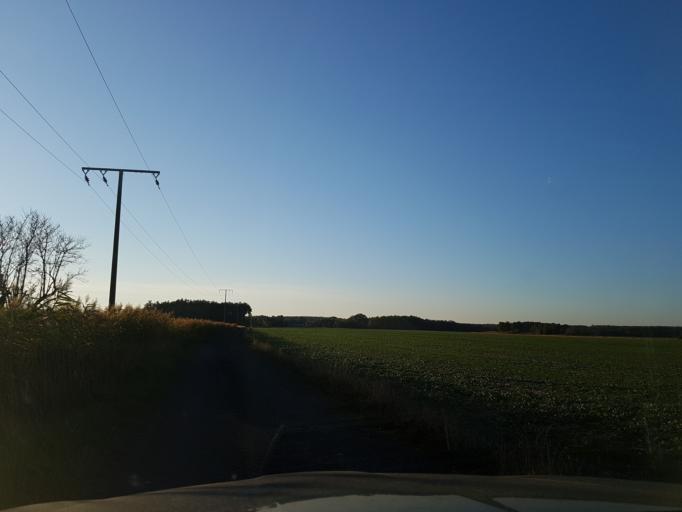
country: DE
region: Brandenburg
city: Bad Liebenwerda
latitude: 51.5463
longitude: 13.3946
